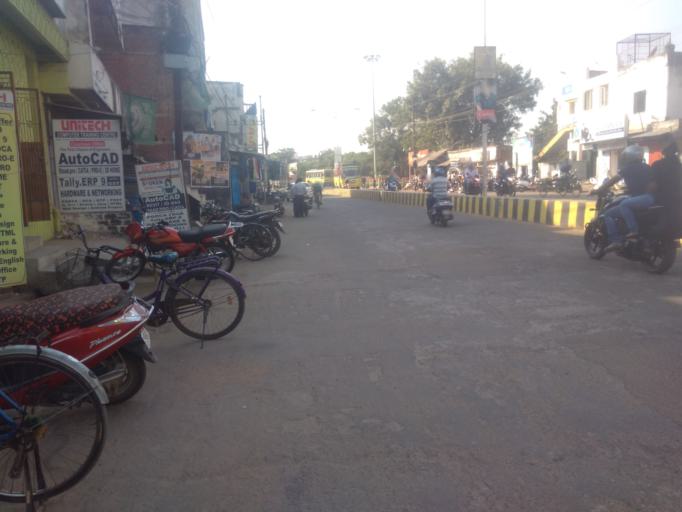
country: IN
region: Odisha
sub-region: Ganjam
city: Brahmapur
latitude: 19.3090
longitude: 84.7905
